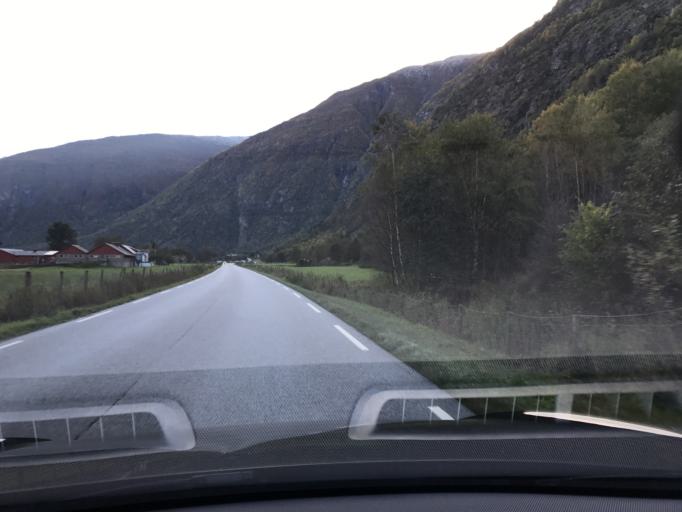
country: NO
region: Sogn og Fjordane
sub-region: Laerdal
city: Laerdalsoyri
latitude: 61.0883
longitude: 7.5129
